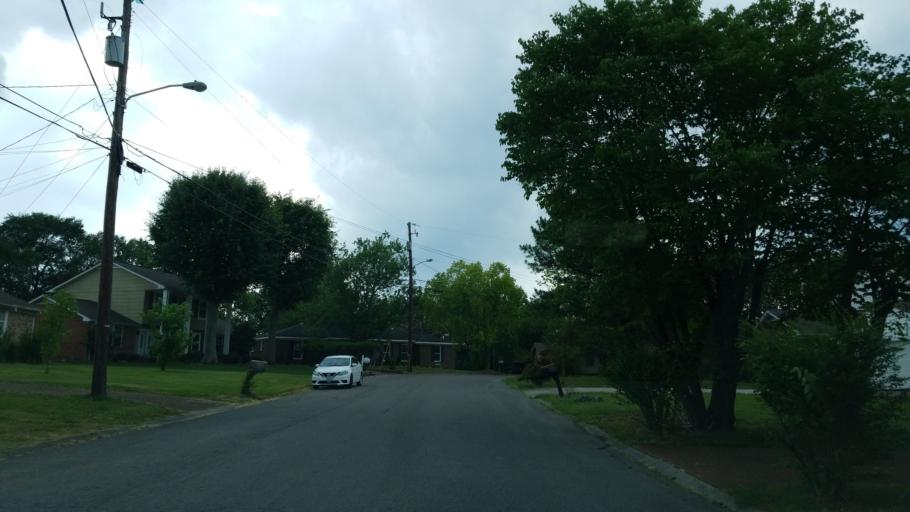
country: US
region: Tennessee
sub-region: Rutherford County
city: La Vergne
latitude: 36.0956
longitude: -86.6103
